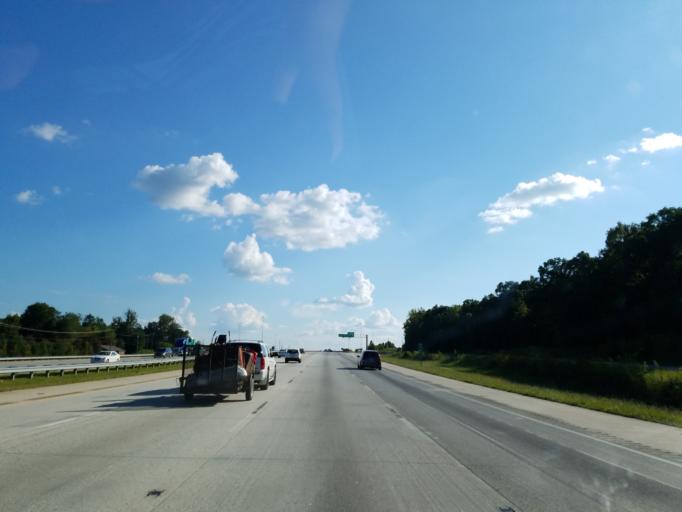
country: US
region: North Carolina
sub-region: Rowan County
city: Spencer
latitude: 35.7015
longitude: -80.3990
